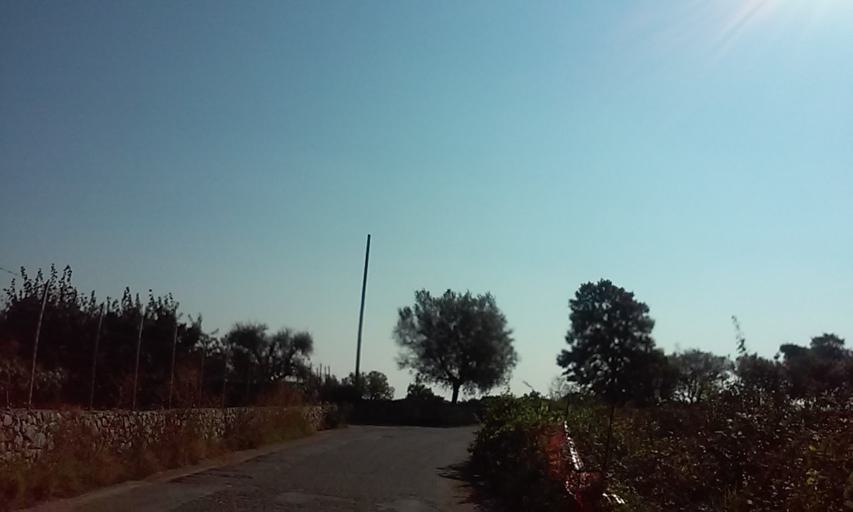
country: IT
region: Apulia
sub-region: Provincia di Brindisi
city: Cisternino
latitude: 40.7035
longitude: 17.4217
